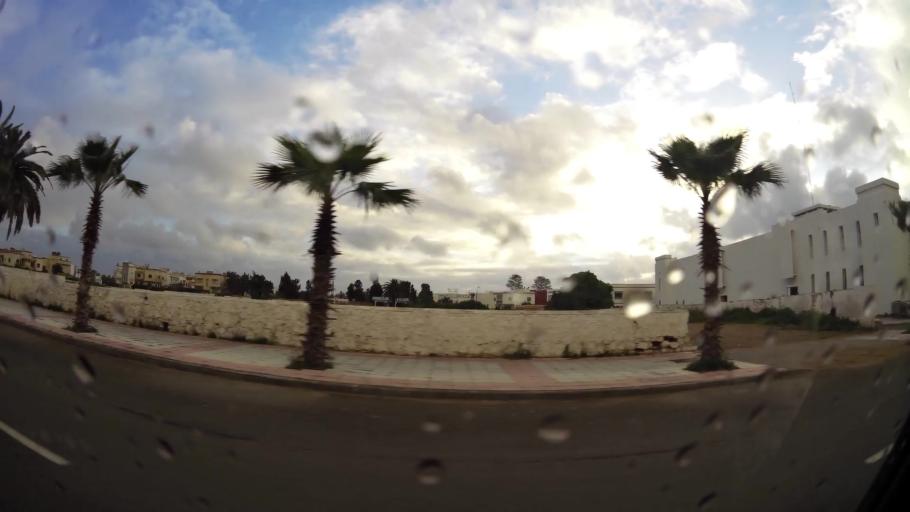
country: MA
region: Doukkala-Abda
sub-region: El-Jadida
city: El Jadida
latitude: 33.2443
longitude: -8.5053
